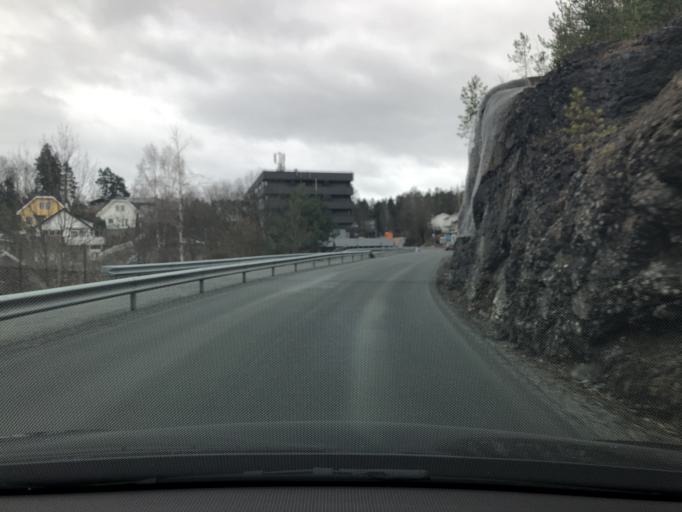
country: NO
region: Akershus
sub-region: Baerum
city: Sandvika
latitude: 59.8719
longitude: 10.5164
